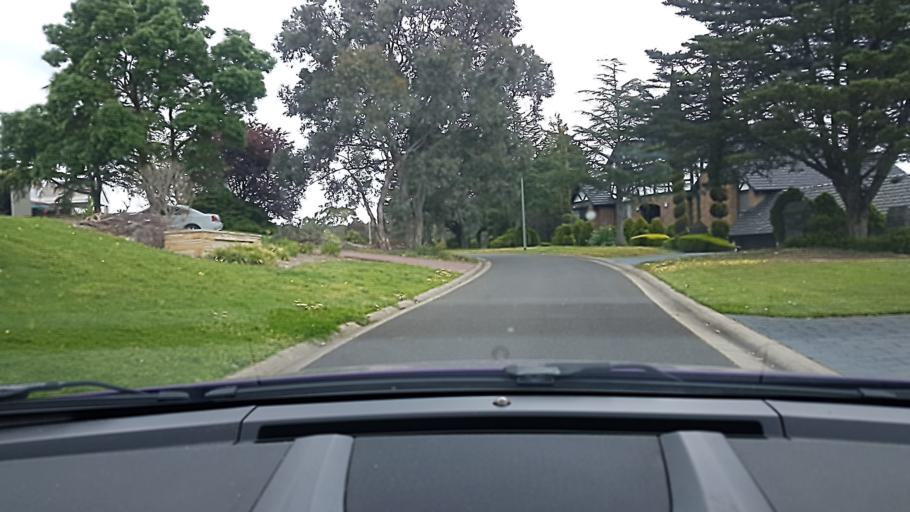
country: AU
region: Victoria
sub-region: Nillumbik
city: Eltham
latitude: -37.7515
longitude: 145.1423
